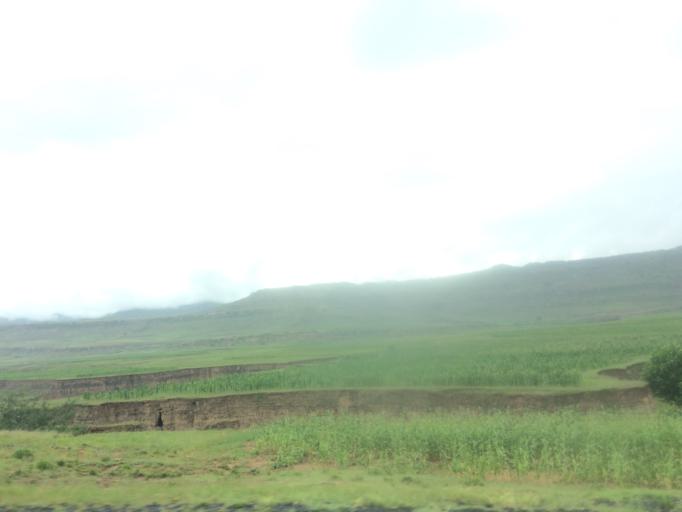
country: LS
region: Mafeteng
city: Mafeteng
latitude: -29.7276
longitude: 27.5004
